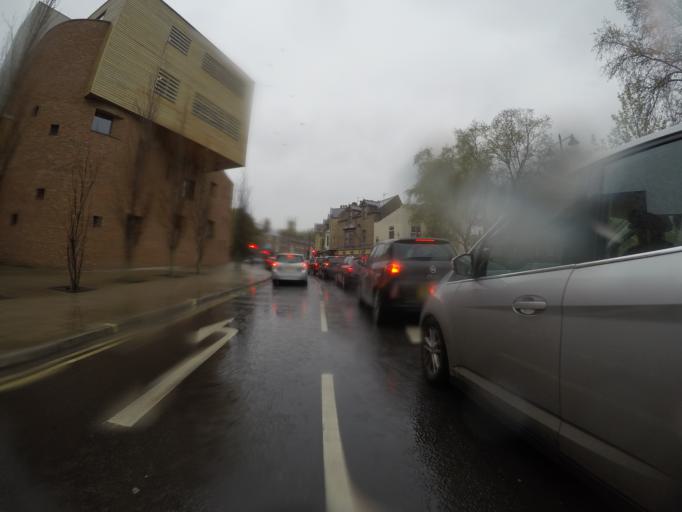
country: GB
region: England
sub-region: City of York
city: York
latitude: 53.9658
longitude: -1.0832
